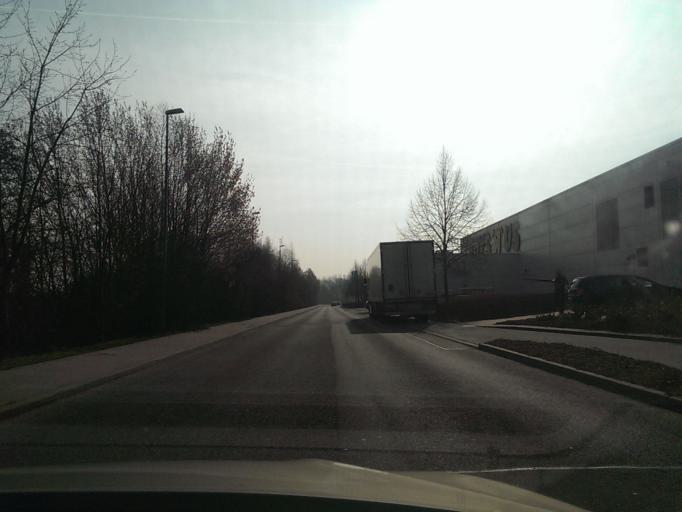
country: DE
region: Saxony
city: Wittgensdorf
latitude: 50.8667
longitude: 12.8660
